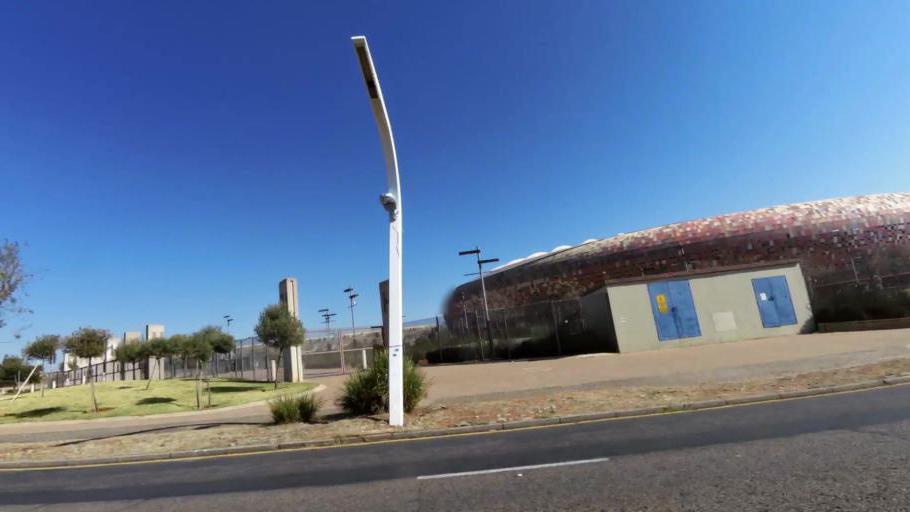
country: ZA
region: Gauteng
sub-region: City of Johannesburg Metropolitan Municipality
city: Johannesburg
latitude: -26.2359
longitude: 27.9854
